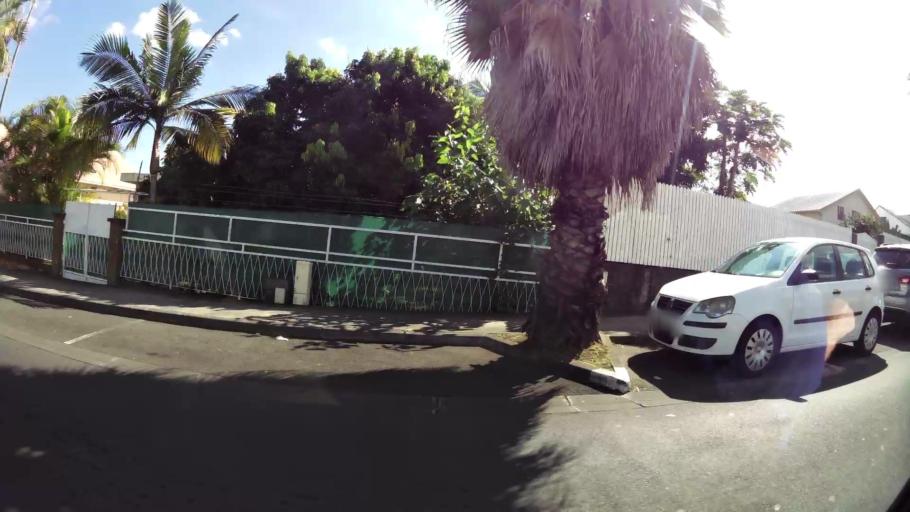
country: RE
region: Reunion
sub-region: Reunion
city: Le Tampon
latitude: -21.2818
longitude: 55.5105
